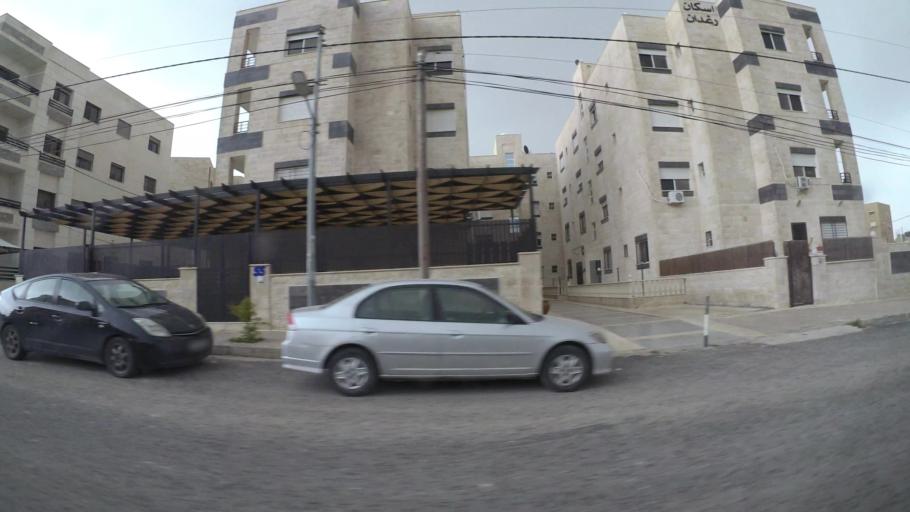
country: JO
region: Amman
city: Umm as Summaq
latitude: 31.8818
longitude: 35.8536
